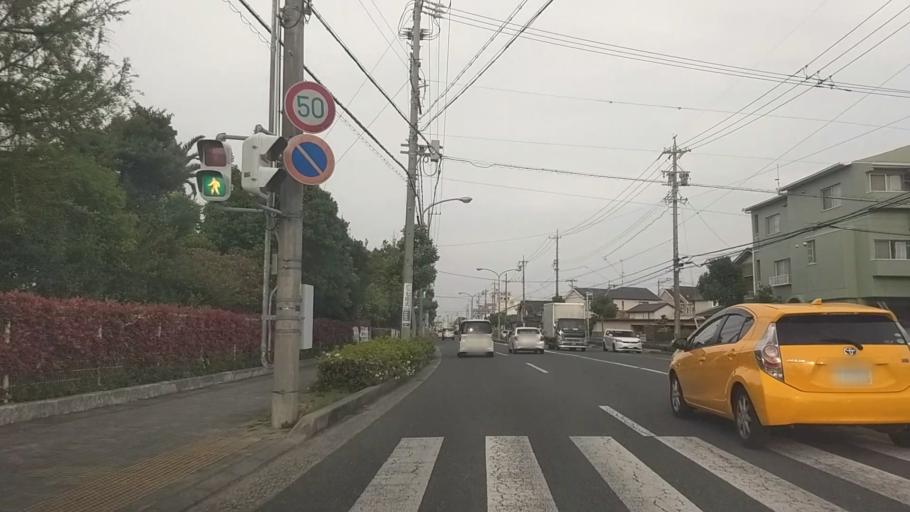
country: JP
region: Shizuoka
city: Hamamatsu
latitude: 34.7187
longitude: 137.7118
